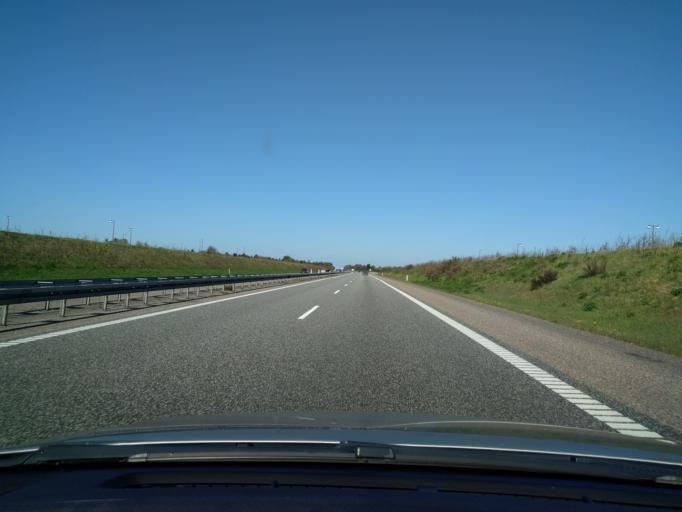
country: DK
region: South Denmark
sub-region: Vejle Kommune
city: Jelling
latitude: 55.8360
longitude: 9.3979
